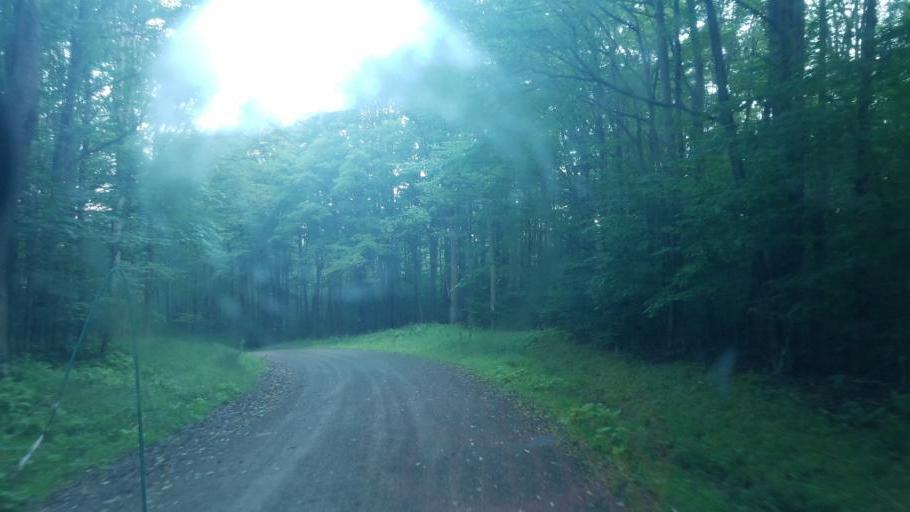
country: US
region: Pennsylvania
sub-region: Potter County
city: Galeton
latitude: 41.8721
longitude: -77.8029
